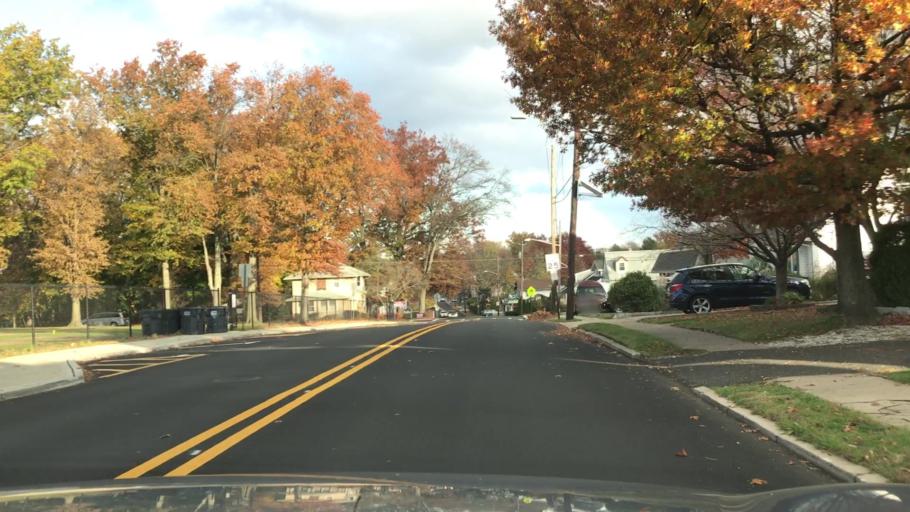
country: US
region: New Jersey
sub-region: Bergen County
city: Bergenfield
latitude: 40.9277
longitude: -74.0042
